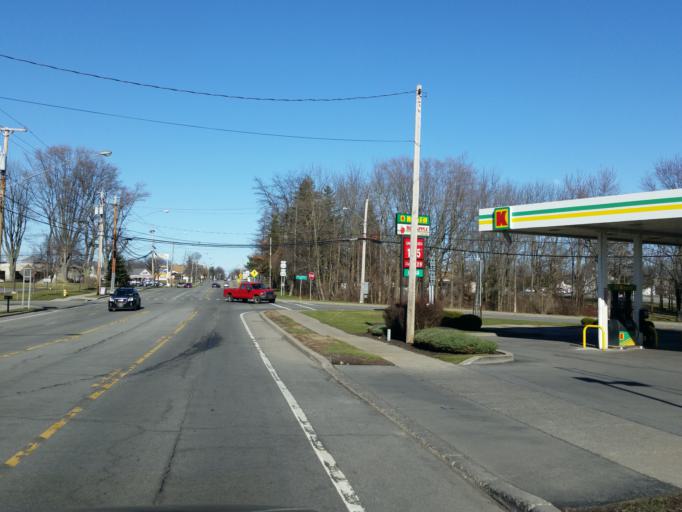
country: US
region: New York
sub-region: Monroe County
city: Scottsville
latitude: 43.1030
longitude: -77.7546
